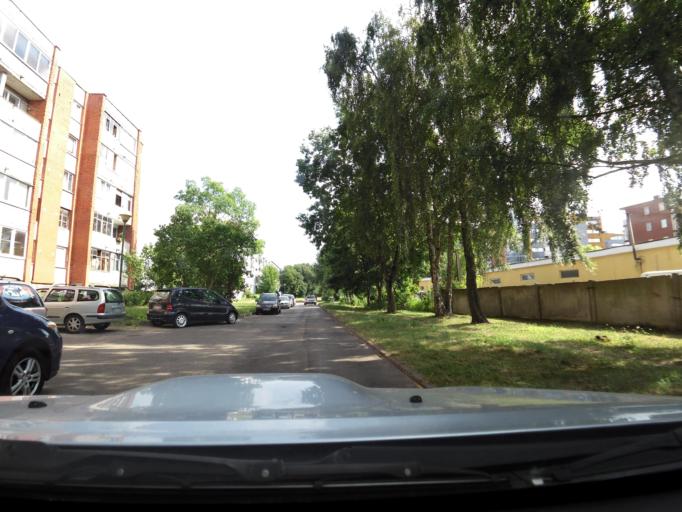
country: LT
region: Klaipedos apskritis
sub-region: Klaipeda
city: Klaipeda
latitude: 55.6959
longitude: 21.1459
